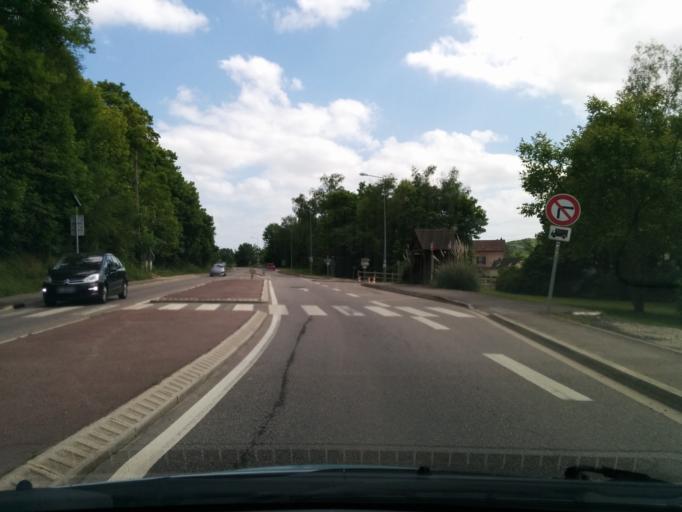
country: FR
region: Ile-de-France
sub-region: Departement des Yvelines
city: Aulnay-sur-Mauldre
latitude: 48.9387
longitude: 1.8410
